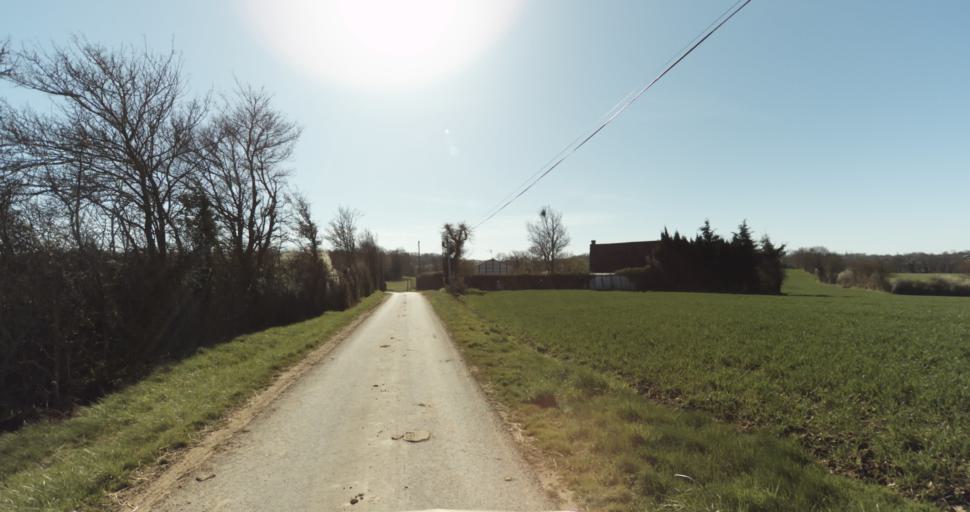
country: FR
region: Lower Normandy
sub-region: Departement de l'Orne
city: Trun
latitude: 48.9153
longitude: 0.0422
